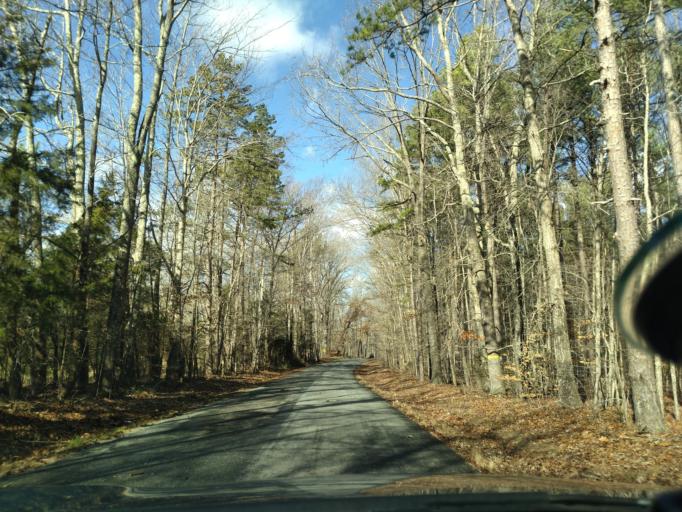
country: US
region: Virginia
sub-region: Nottoway County
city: Crewe
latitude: 37.1758
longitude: -78.2640
